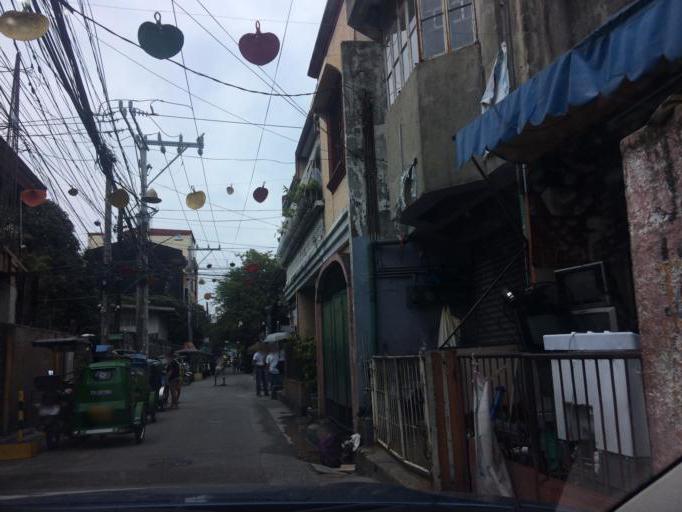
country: PH
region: Metro Manila
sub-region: Makati City
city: Makati City
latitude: 14.5445
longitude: 121.0075
